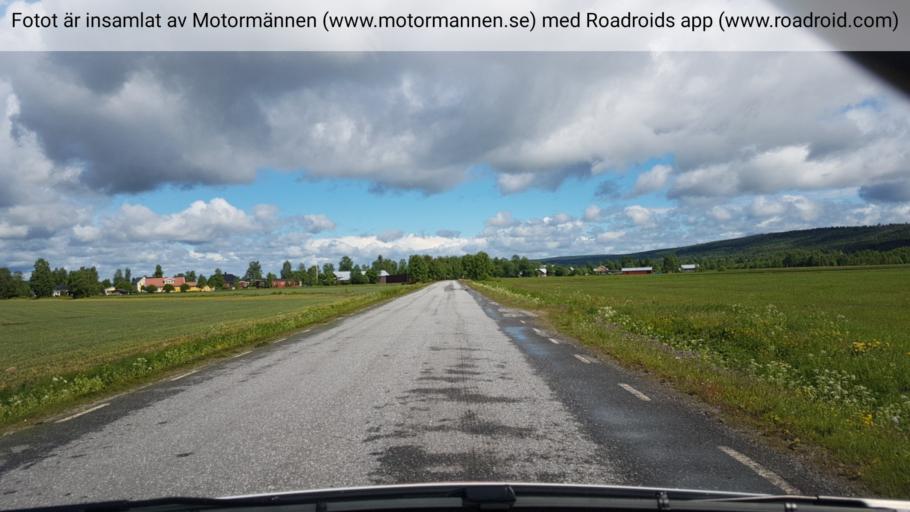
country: SE
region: Vaesterbotten
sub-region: Vannas Kommun
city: Vannasby
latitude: 63.9332
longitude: 19.8571
